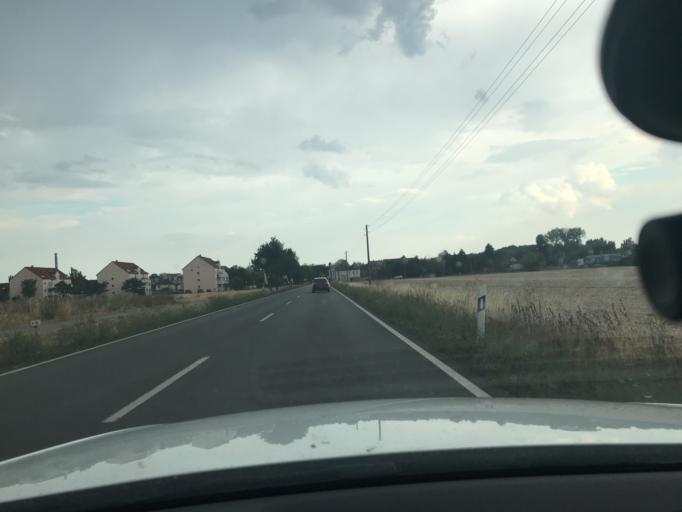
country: DE
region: Saxony
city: Markranstadt
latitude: 51.3095
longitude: 12.2148
